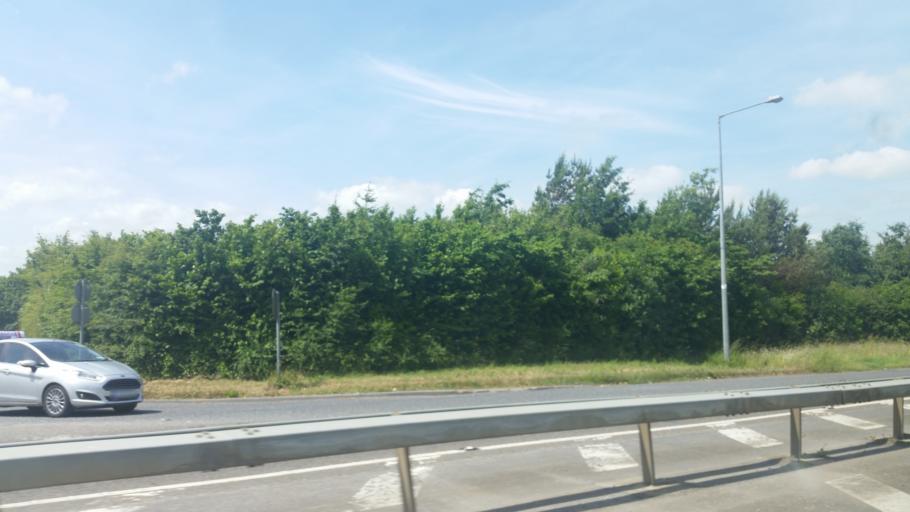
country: IE
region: Leinster
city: Balrothery
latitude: 53.5519
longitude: -6.2099
